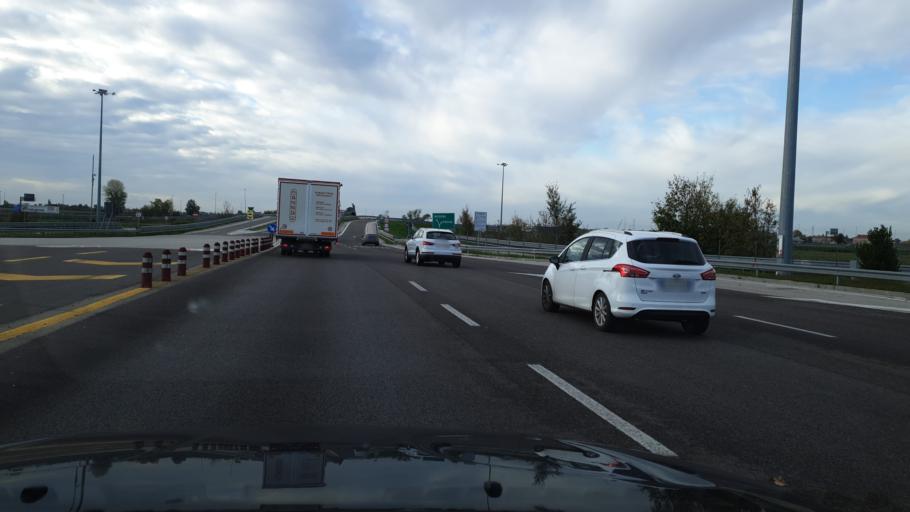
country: IT
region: Veneto
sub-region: Provincia di Rovigo
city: Villamarzana
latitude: 45.0223
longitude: 11.6983
